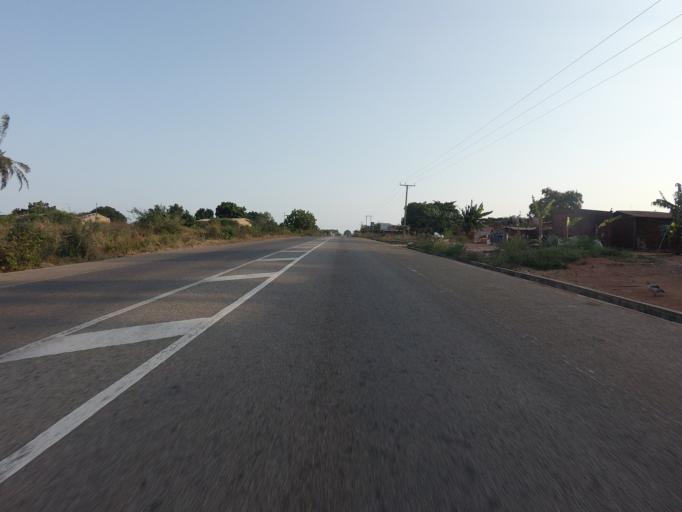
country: GH
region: Volta
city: Anloga
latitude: 6.0181
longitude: 0.5994
